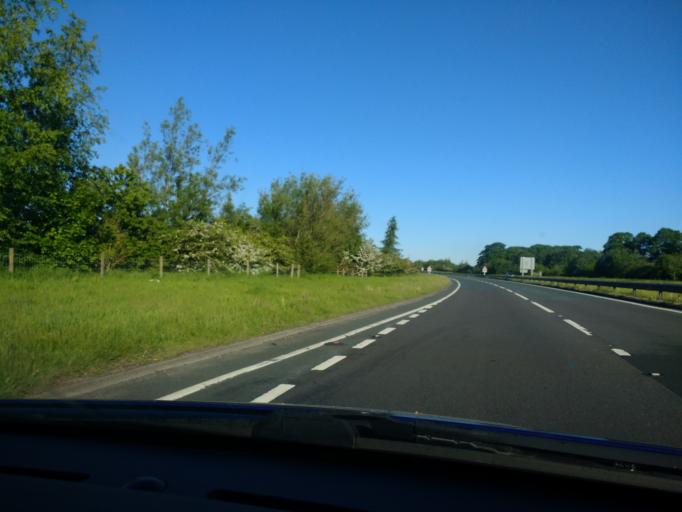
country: GB
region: England
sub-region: Cumbria
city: Penrith
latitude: 54.6498
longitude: -2.6289
